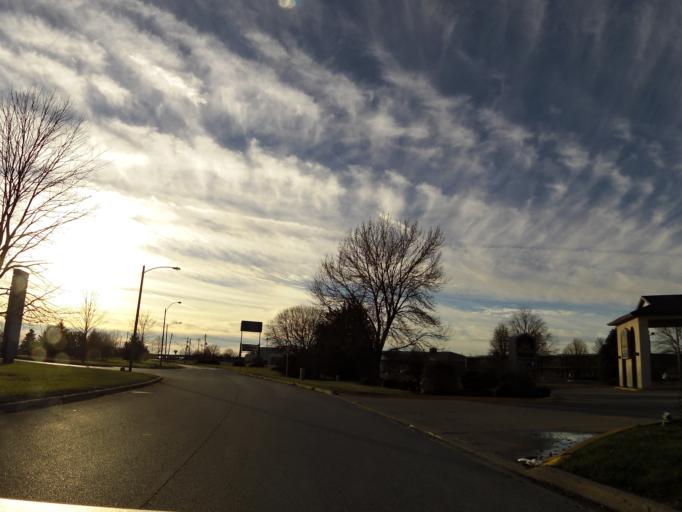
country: US
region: Illinois
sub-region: Vermilion County
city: Danville
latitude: 40.1219
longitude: -87.5424
